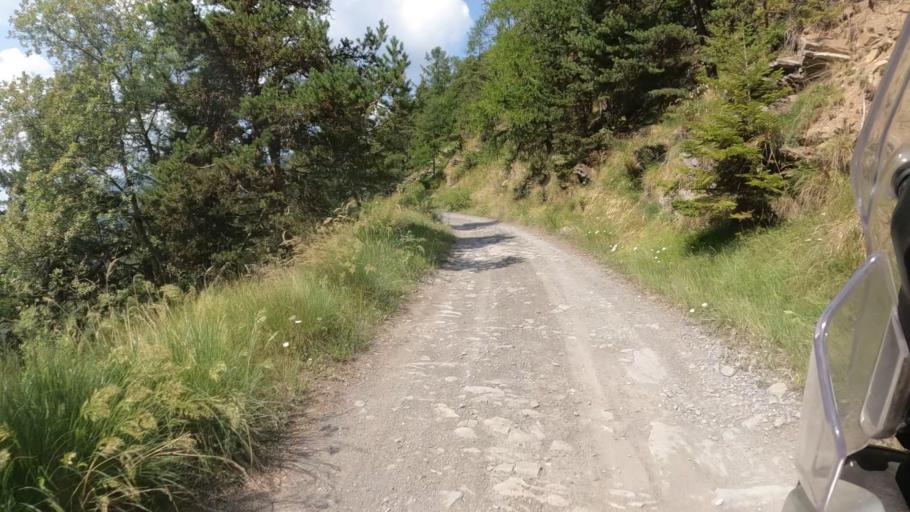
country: IT
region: Piedmont
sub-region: Provincia di Cuneo
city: Briga Alta
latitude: 44.0388
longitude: 7.6898
